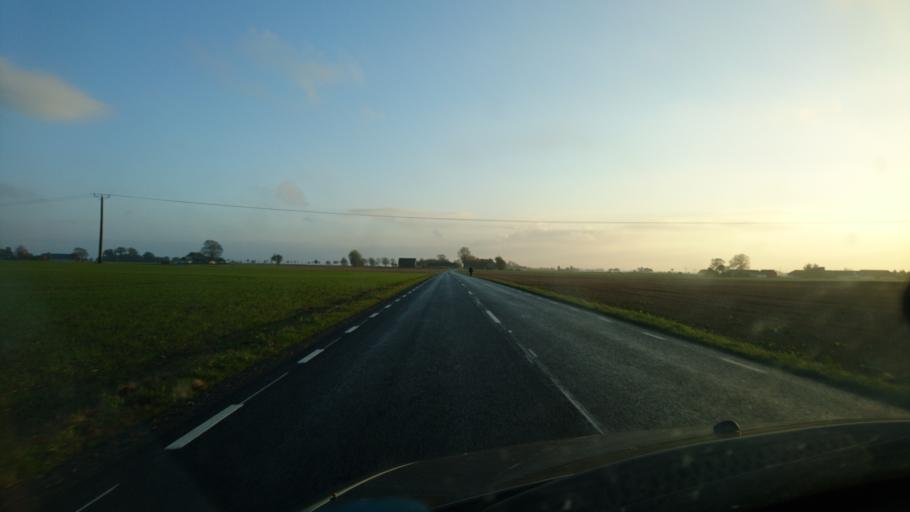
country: SE
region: Skane
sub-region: Simrishamns Kommun
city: Simrishamn
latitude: 55.4480
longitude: 14.1769
